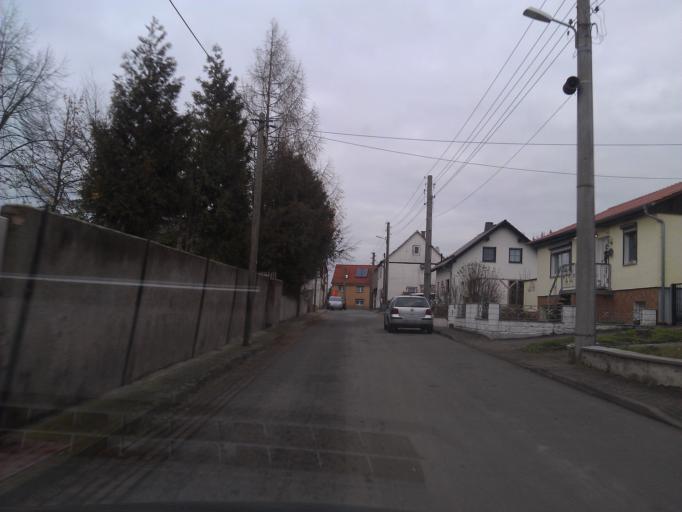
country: DE
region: Thuringia
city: Pferdingsleben
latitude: 50.9690
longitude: 10.8213
